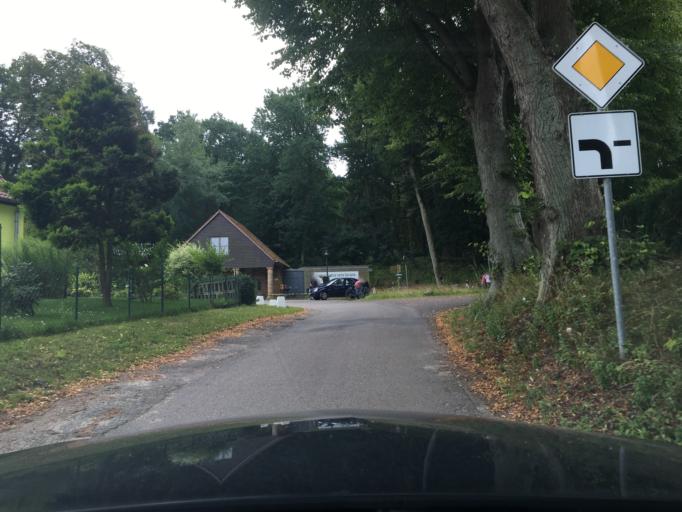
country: DE
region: Mecklenburg-Vorpommern
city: Mollenhagen
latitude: 53.4387
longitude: 12.8399
